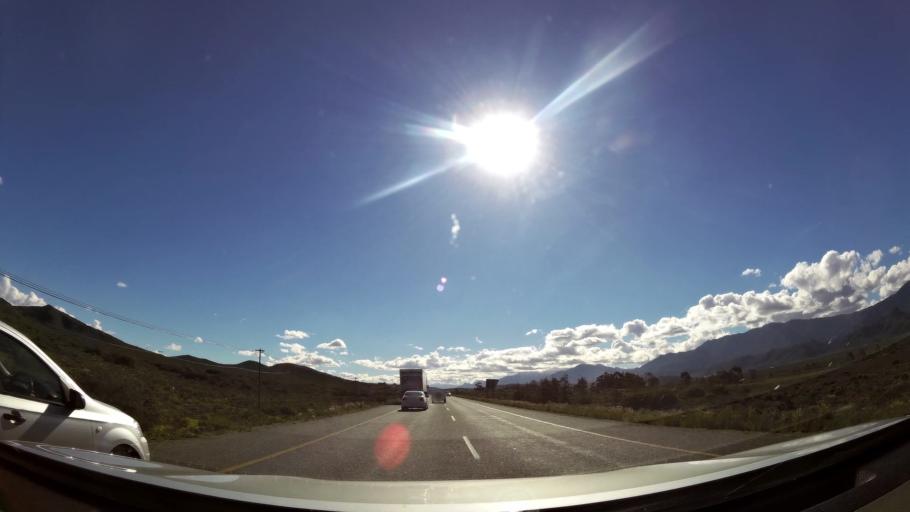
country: ZA
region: Western Cape
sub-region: Cape Winelands District Municipality
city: Ashton
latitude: -33.7659
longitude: 19.7447
